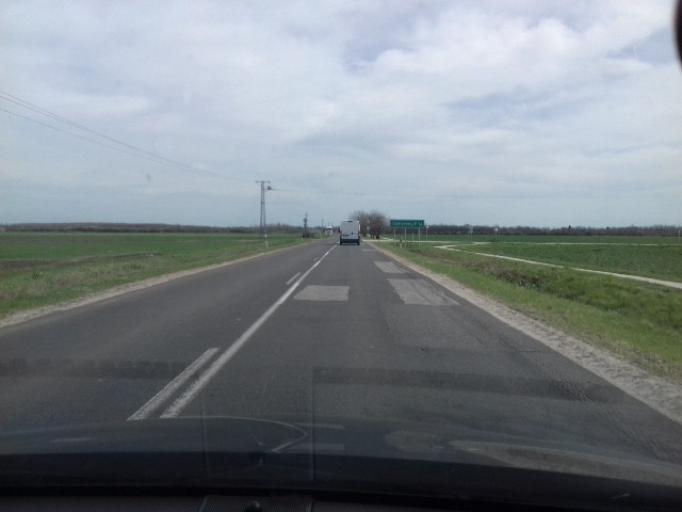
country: HU
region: Jasz-Nagykun-Szolnok
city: Kunszentmarton
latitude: 46.8531
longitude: 20.2406
